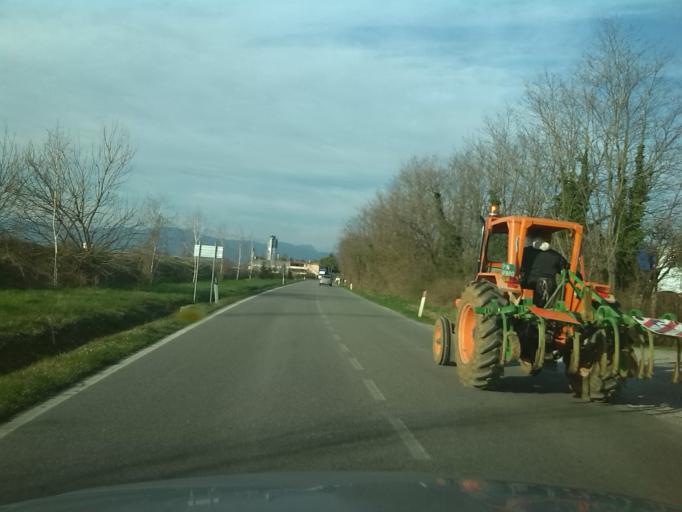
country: IT
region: Friuli Venezia Giulia
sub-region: Provincia di Udine
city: Orsaria
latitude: 46.0298
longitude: 13.3979
